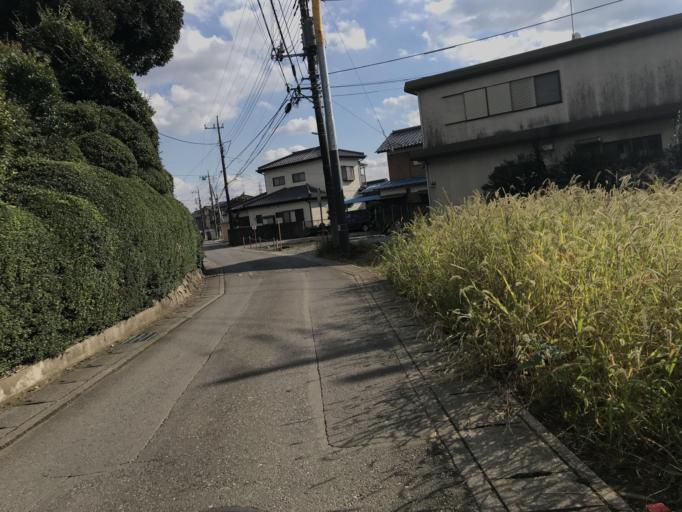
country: JP
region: Tochigi
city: Oyama
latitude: 36.2719
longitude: 139.7655
